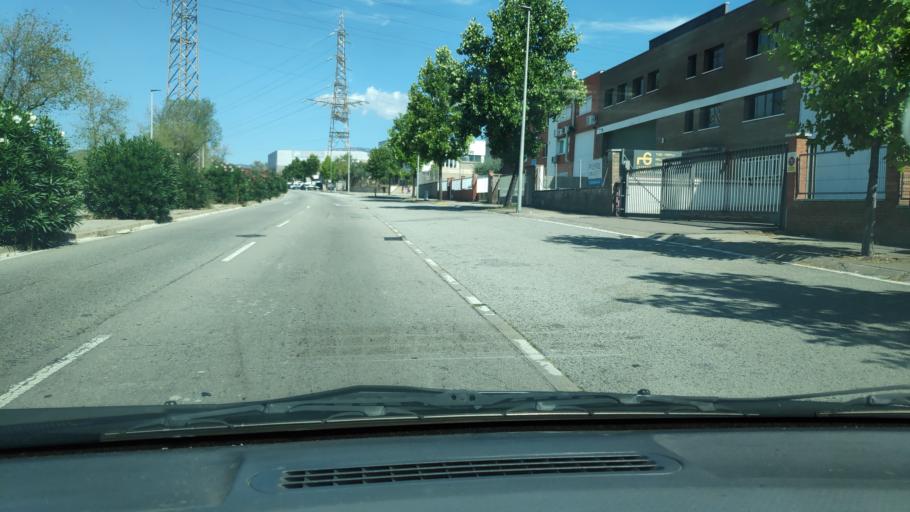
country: ES
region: Catalonia
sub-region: Provincia de Barcelona
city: Terrassa
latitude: 41.5505
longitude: 2.0400
